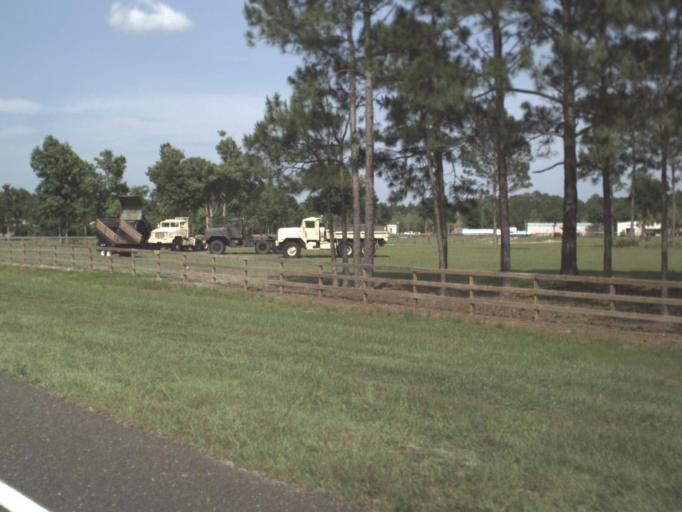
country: US
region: Florida
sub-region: Saint Johns County
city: Saint Augustine Shores
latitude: 29.7624
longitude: -81.4608
